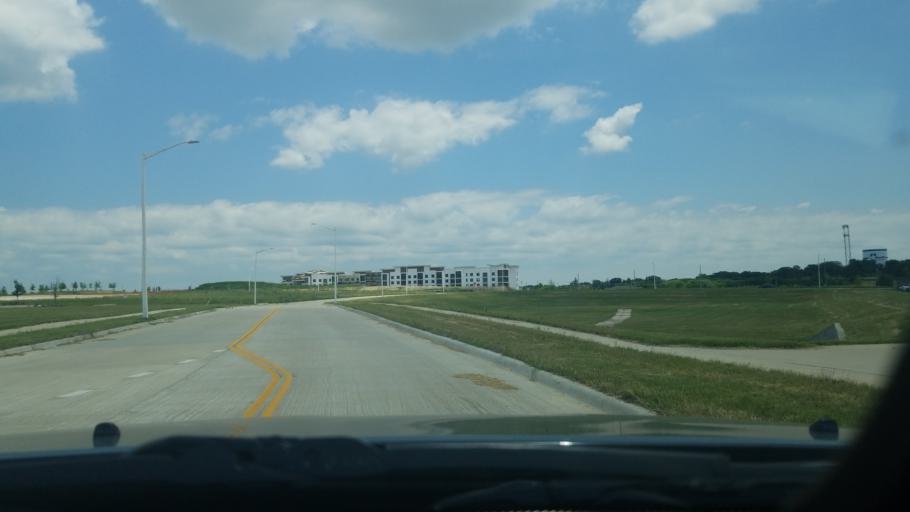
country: US
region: Texas
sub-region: Denton County
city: Denton
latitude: 33.2207
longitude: -97.1686
